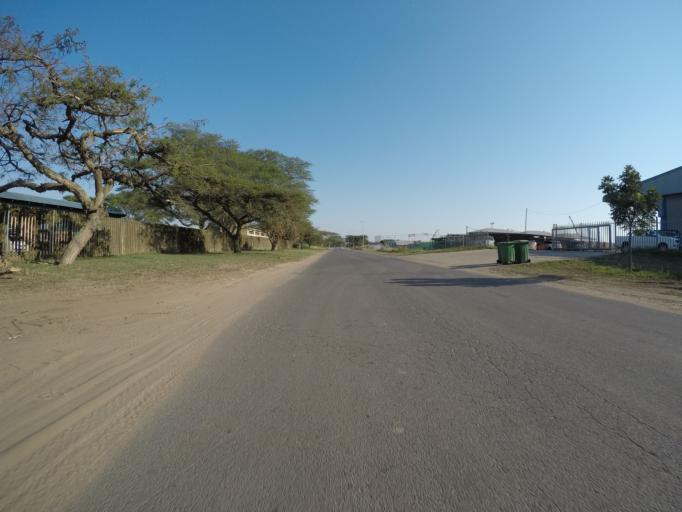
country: ZA
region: KwaZulu-Natal
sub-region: uThungulu District Municipality
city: Richards Bay
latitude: -28.7487
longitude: 32.0218
